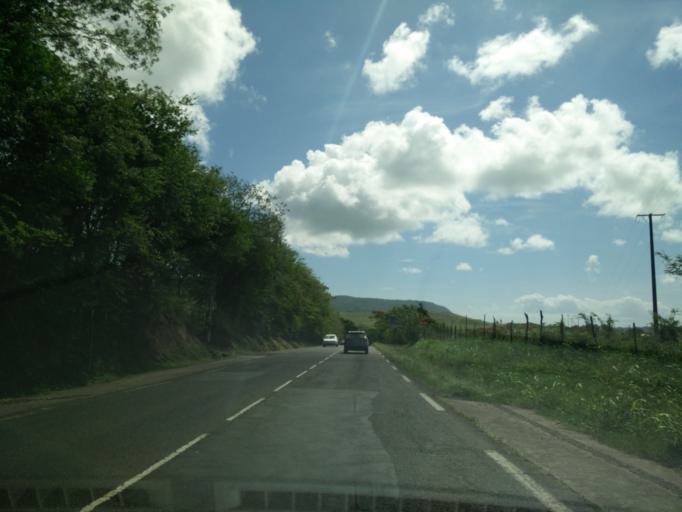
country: MQ
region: Martinique
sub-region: Martinique
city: Les Trois-Ilets
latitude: 14.5283
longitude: -61.0040
